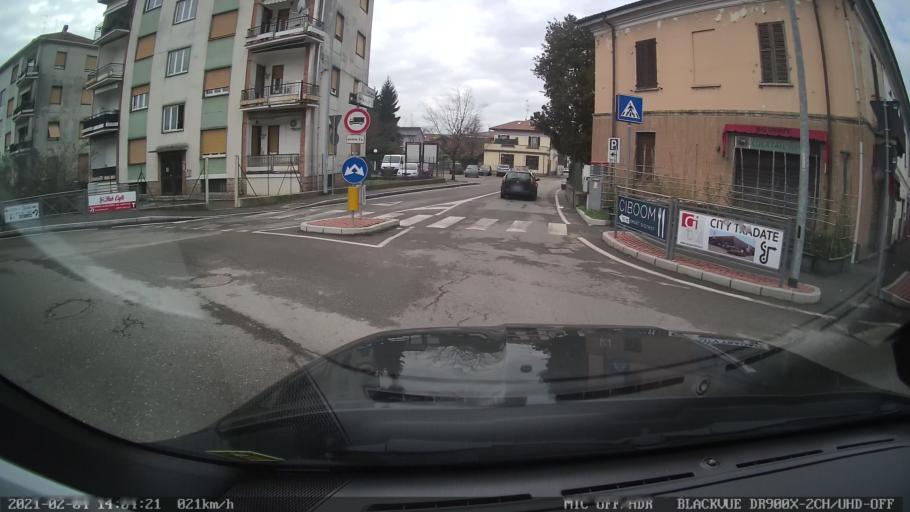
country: IT
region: Lombardy
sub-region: Provincia di Varese
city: Tradate
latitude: 45.7185
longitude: 8.8967
